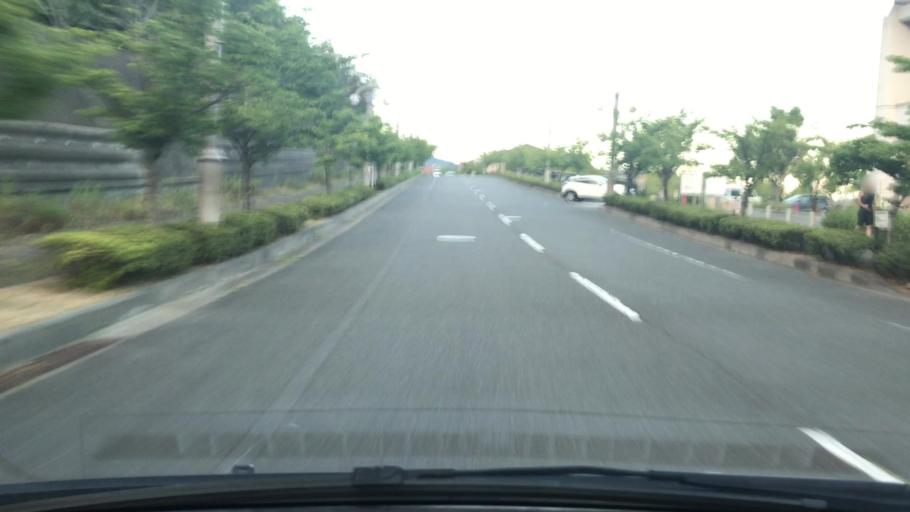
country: JP
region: Hyogo
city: Takarazuka
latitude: 34.8345
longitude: 135.3051
